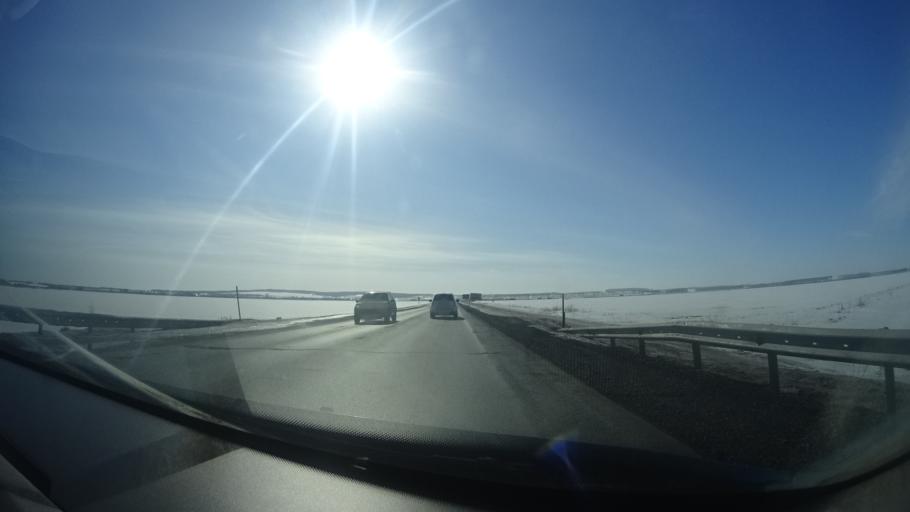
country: RU
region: Bashkortostan
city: Mikhaylovka
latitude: 54.8915
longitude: 55.7207
